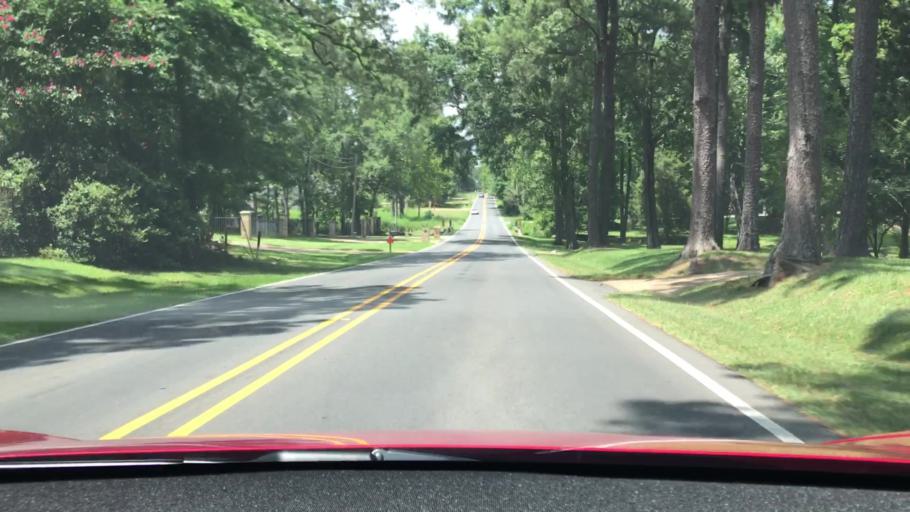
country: US
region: Louisiana
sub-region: Bossier Parish
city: Bossier City
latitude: 32.3762
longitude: -93.7137
